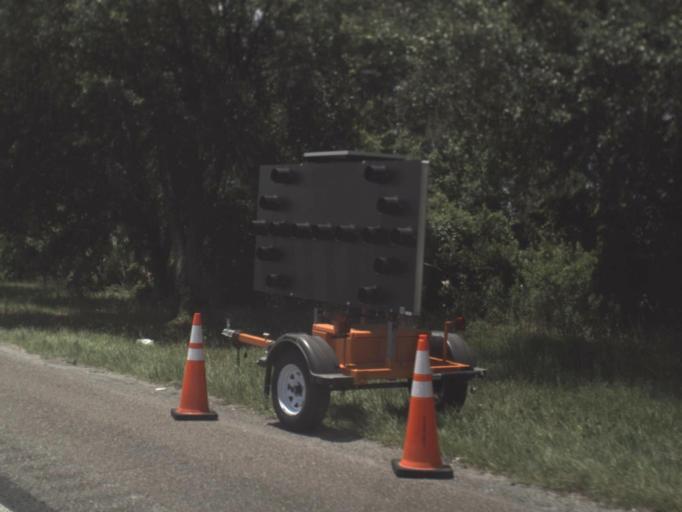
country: US
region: Florida
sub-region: Duval County
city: Jacksonville
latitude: 30.3952
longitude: -81.5617
